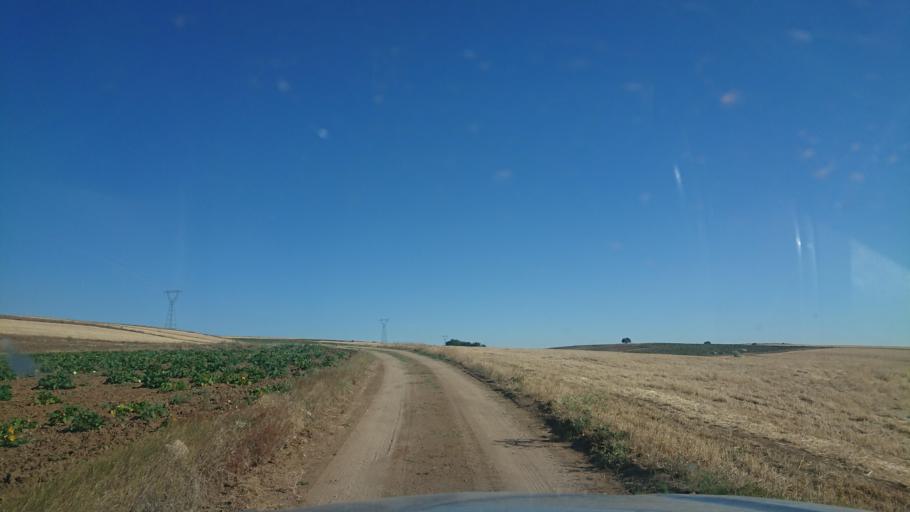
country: TR
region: Aksaray
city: Agacoren
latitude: 38.8342
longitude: 33.9480
